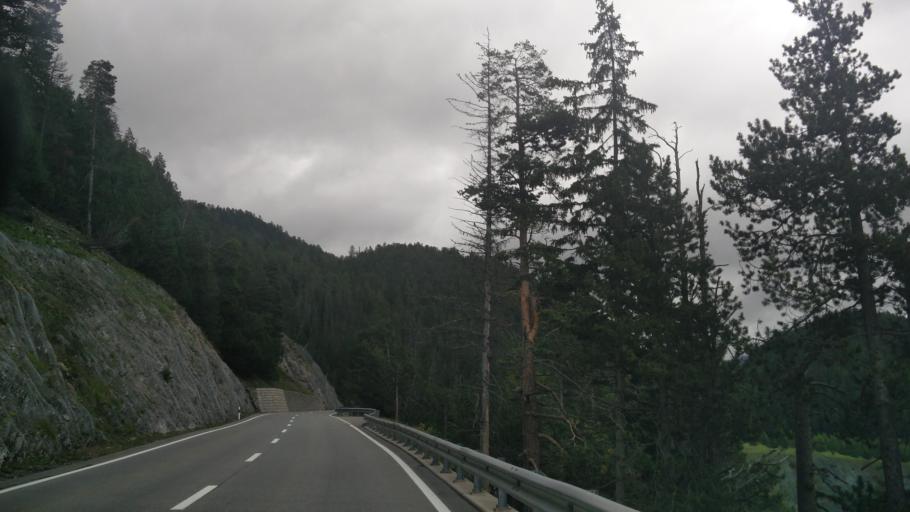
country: CH
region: Grisons
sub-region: Inn District
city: Zernez
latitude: 46.6893
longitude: 10.1406
